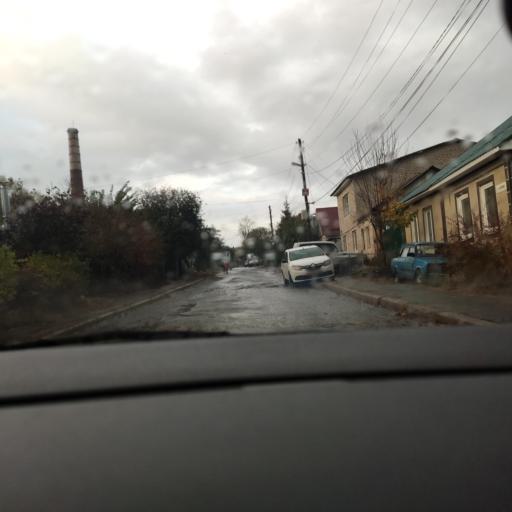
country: RU
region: Voronezj
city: Voronezh
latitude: 51.6721
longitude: 39.1451
